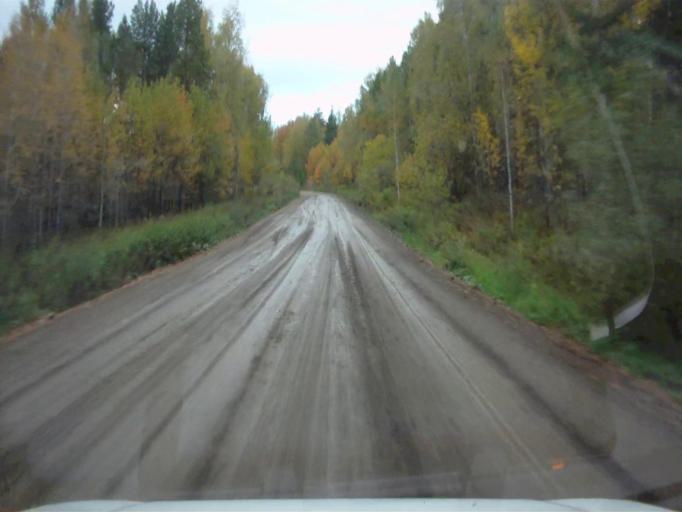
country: RU
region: Chelyabinsk
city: Nyazepetrovsk
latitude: 56.1187
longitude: 59.3691
